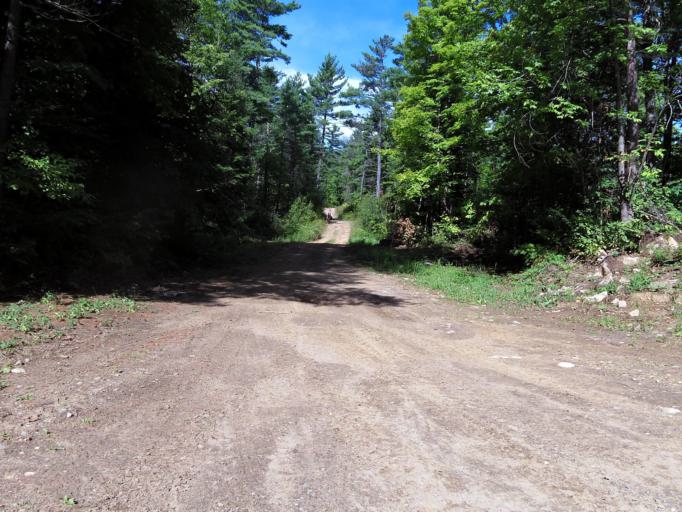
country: CA
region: Ontario
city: Renfrew
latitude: 45.1277
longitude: -76.7267
